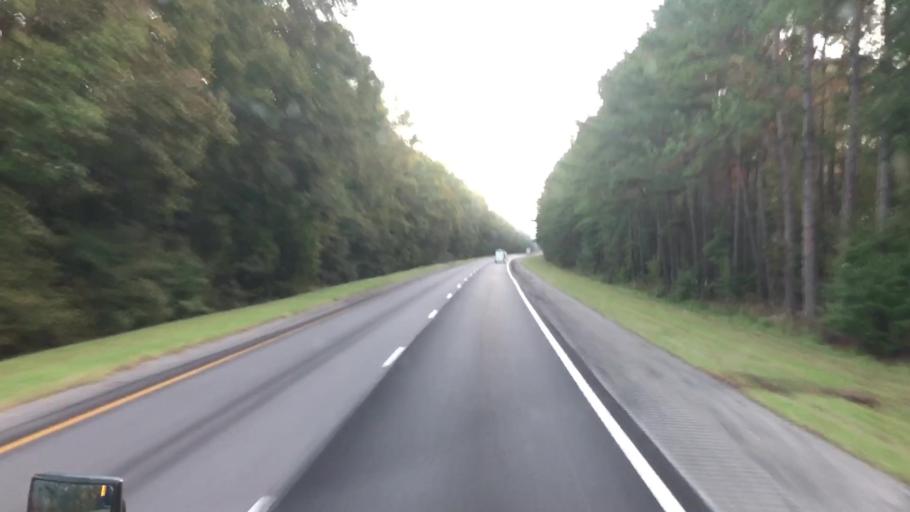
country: US
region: South Carolina
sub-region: Orangeburg County
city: Holly Hill
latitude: 33.5523
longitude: -80.4054
